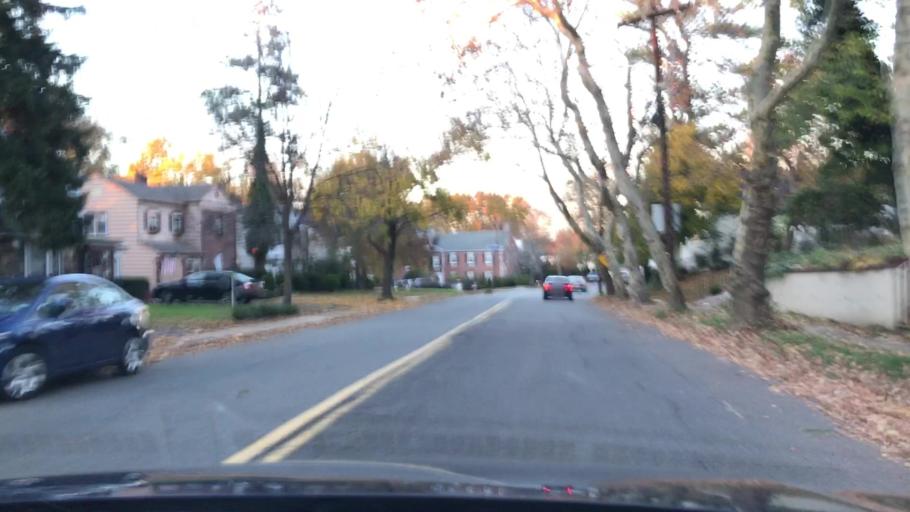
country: US
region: New Jersey
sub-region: Bergen County
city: Bogota
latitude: 40.8843
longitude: -74.0218
